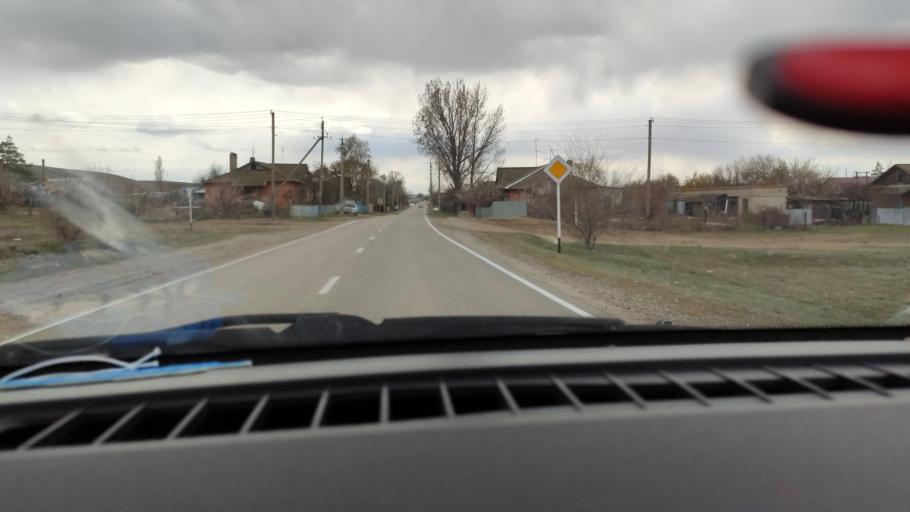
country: RU
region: Saratov
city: Privolzhskiy
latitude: 51.2074
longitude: 45.9183
